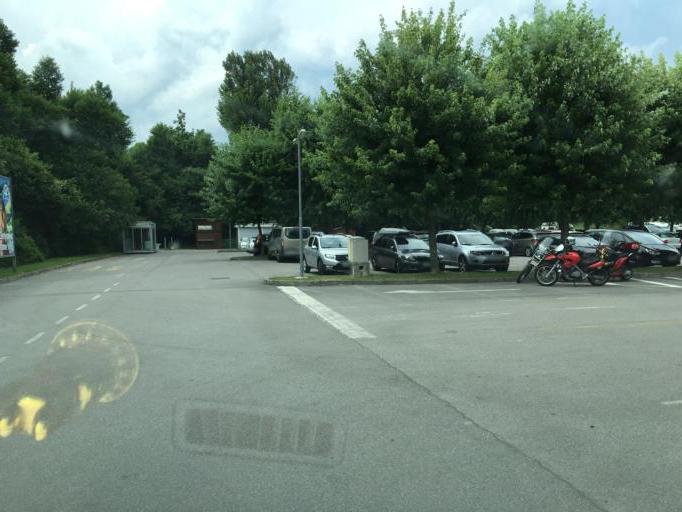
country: SI
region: Postojna
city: Postojna
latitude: 45.7809
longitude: 14.2015
